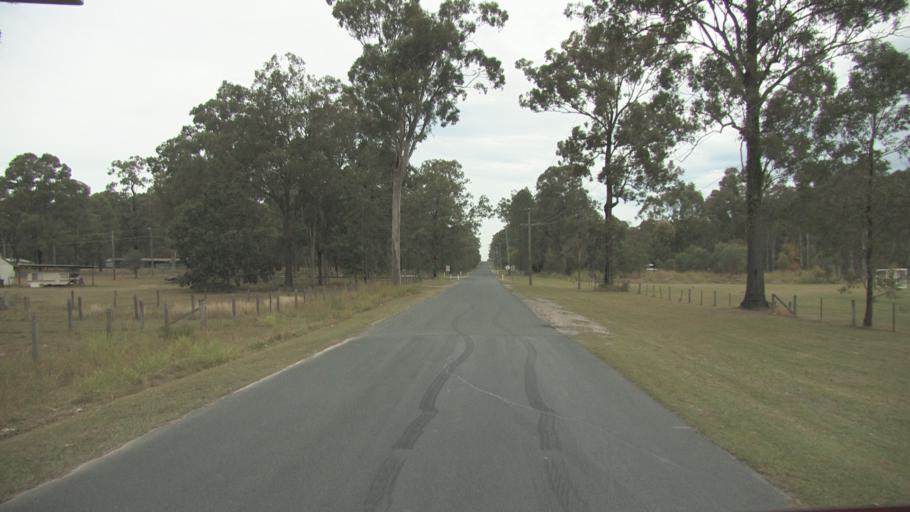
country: AU
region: Queensland
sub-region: Logan
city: Chambers Flat
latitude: -27.7904
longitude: 153.1208
